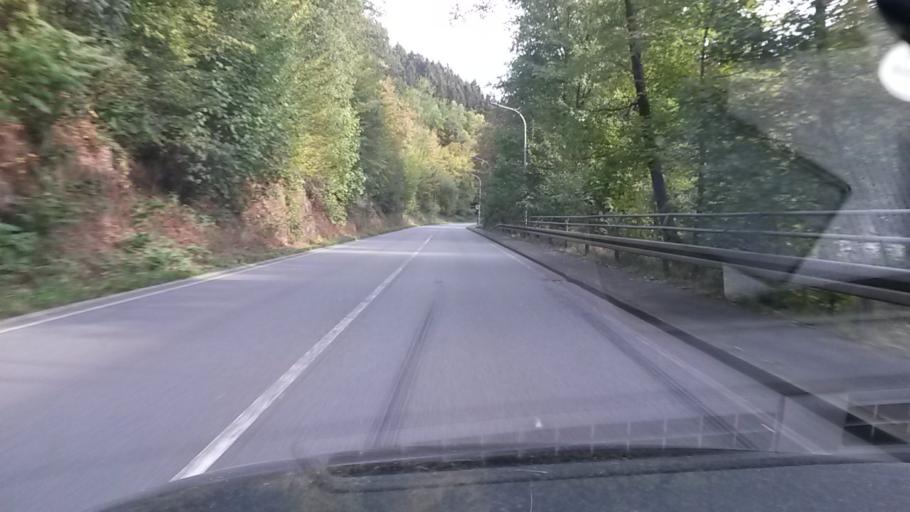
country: DE
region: North Rhine-Westphalia
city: Werdohl
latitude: 51.2408
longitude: 7.7200
